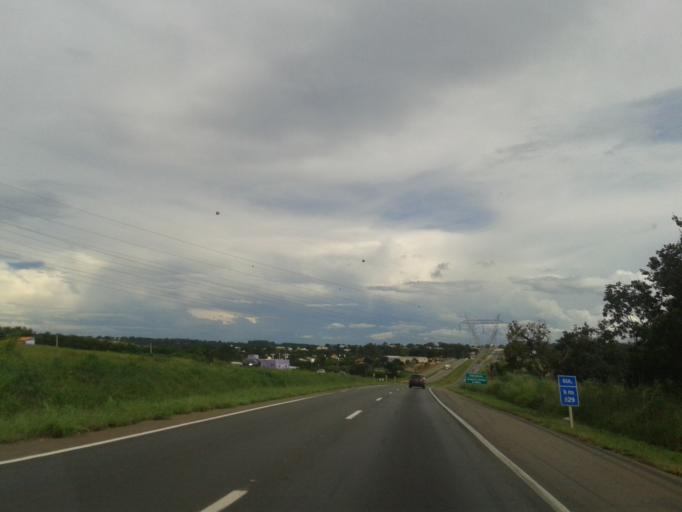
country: BR
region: Goias
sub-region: Hidrolandia
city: Hidrolandia
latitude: -16.9531
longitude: -49.2439
